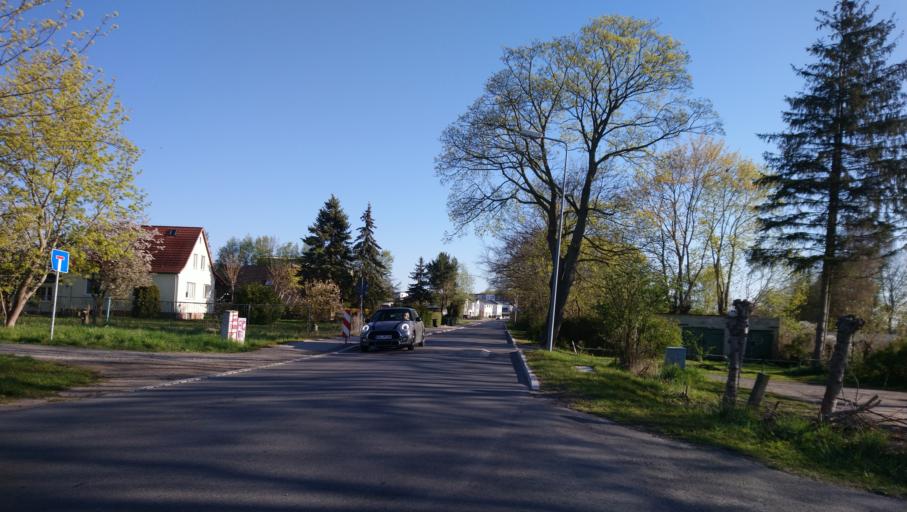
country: DE
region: Mecklenburg-Vorpommern
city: Papendorf
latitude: 54.0621
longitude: 12.1294
